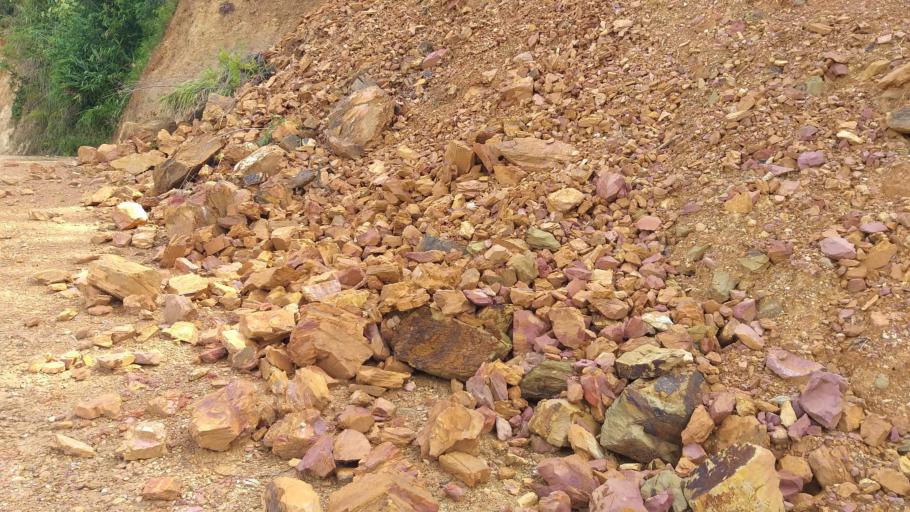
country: LA
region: Phongsali
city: Khoa
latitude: 21.2554
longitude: 102.5901
